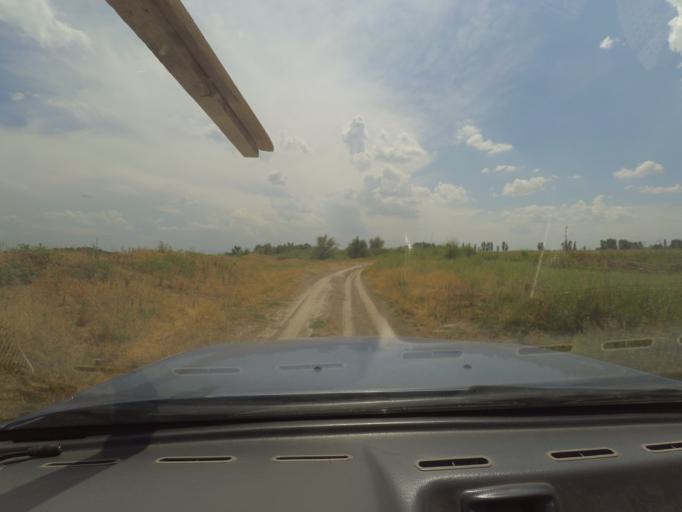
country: TJ
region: Viloyati Sughd
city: Buston
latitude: 40.5388
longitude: 69.0787
